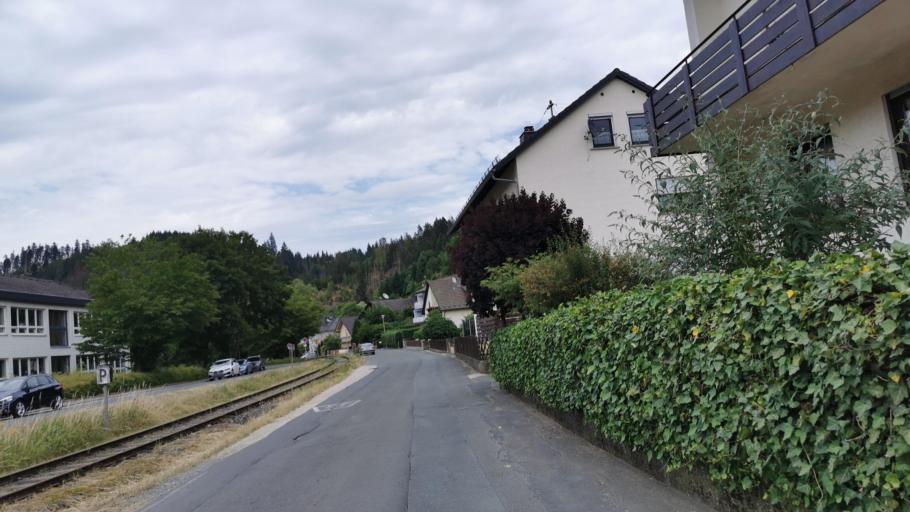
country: DE
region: Bavaria
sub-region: Upper Franconia
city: Steinwiesen
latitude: 50.2935
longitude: 11.4648
